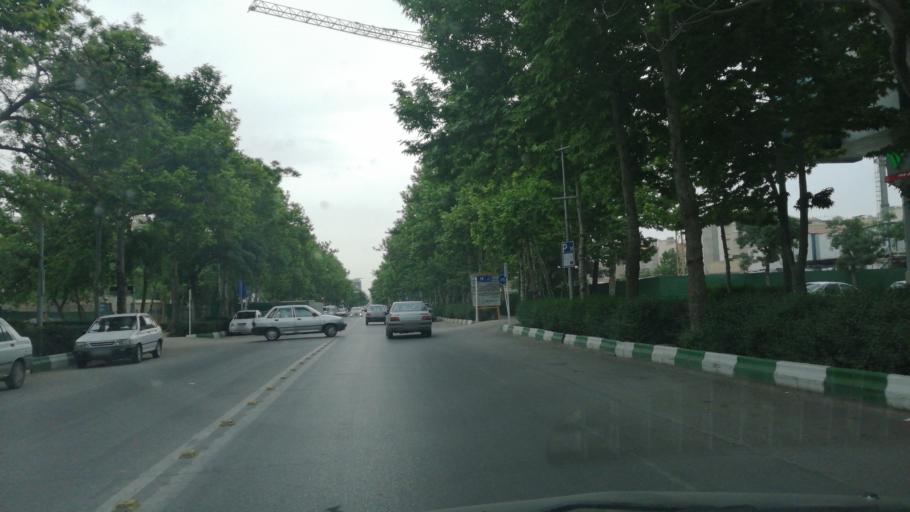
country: IR
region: Razavi Khorasan
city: Mashhad
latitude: 36.2875
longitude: 59.5752
